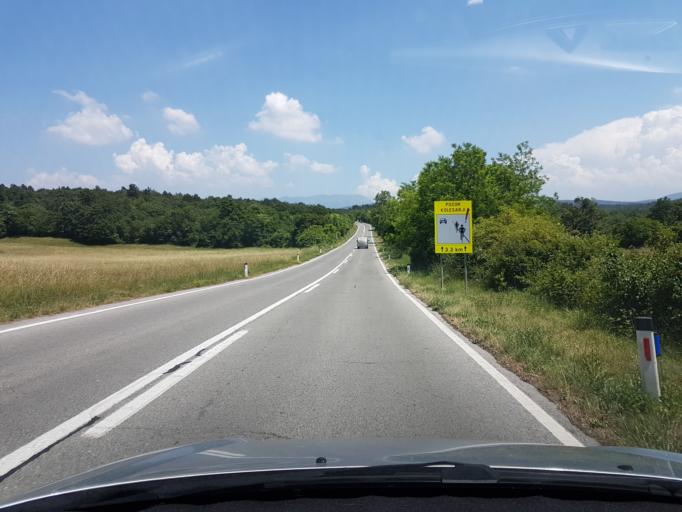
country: SI
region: Sezana
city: Sezana
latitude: 45.7159
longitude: 13.8870
